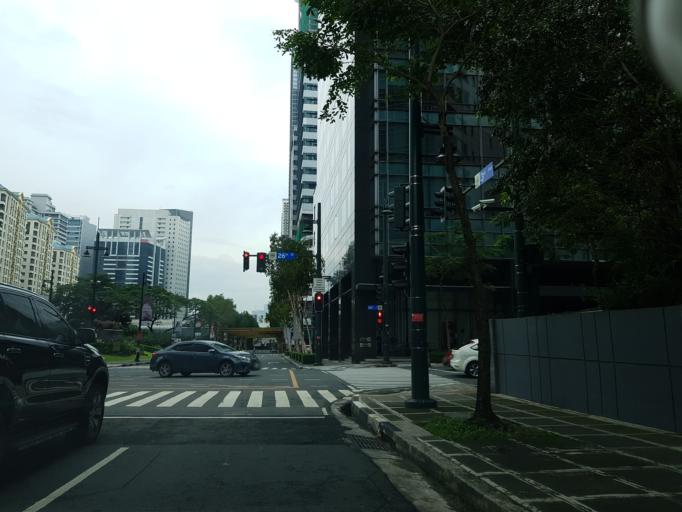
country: PH
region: Metro Manila
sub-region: Makati City
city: Makati City
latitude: 14.5490
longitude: 121.0450
